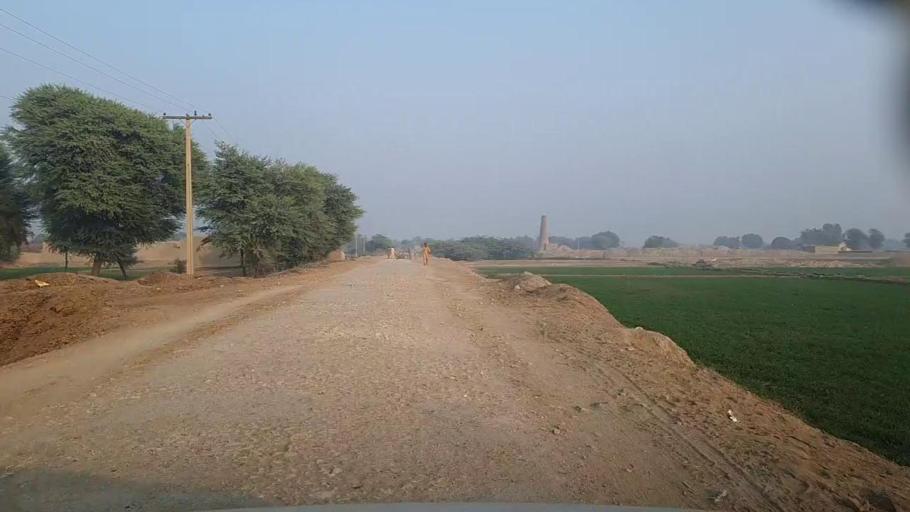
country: PK
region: Sindh
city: Bozdar
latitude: 27.0819
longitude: 68.5347
